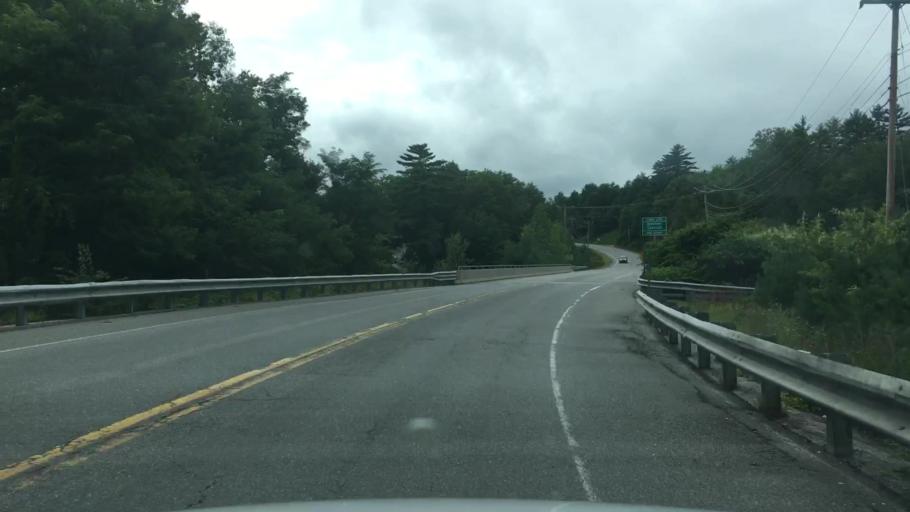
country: US
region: Maine
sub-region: York County
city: Cornish
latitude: 43.8075
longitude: -70.7800
